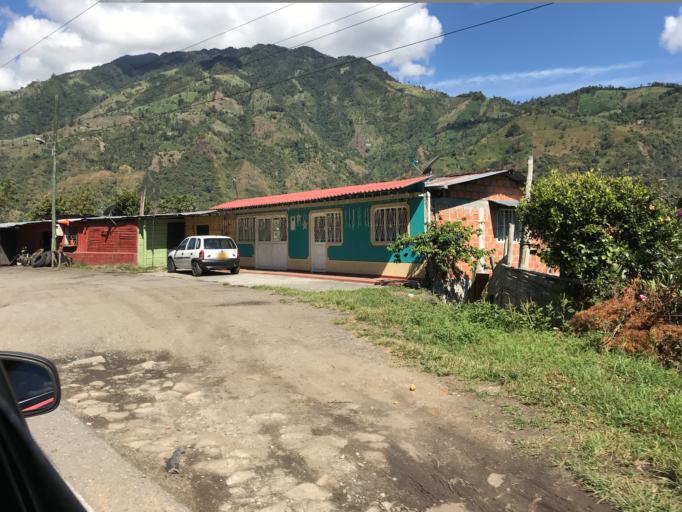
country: CO
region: Tolima
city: Cajamarca
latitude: 4.4425
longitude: -75.4072
